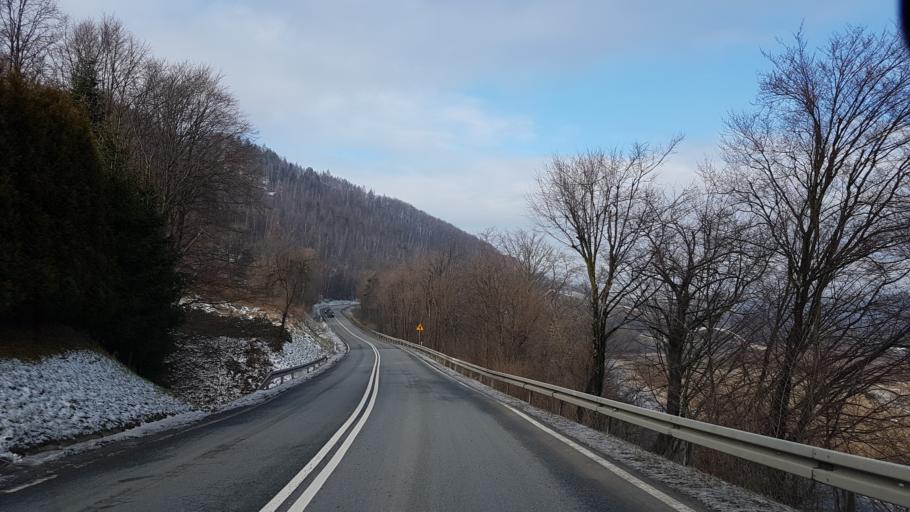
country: PL
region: Lesser Poland Voivodeship
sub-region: Powiat nowosadecki
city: Rytro
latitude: 49.4762
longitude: 20.6829
